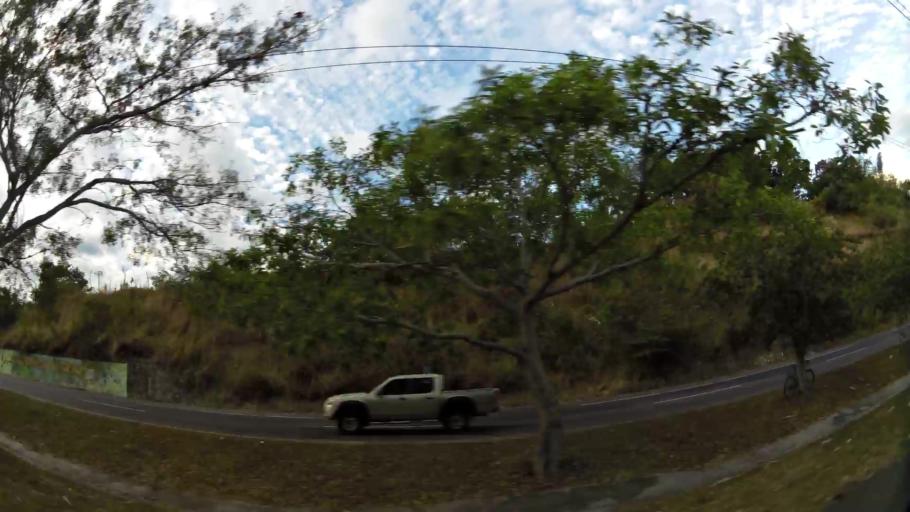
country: SV
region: San Vicente
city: San Vicente
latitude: 13.6701
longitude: -88.8325
